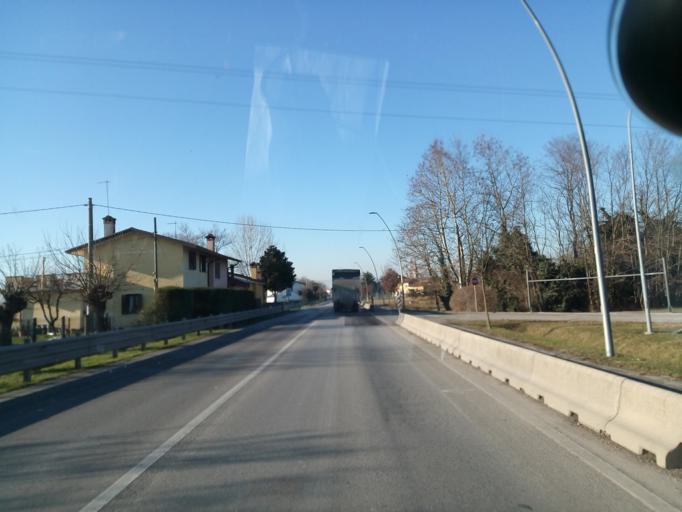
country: IT
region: Veneto
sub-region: Provincia di Treviso
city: Resana
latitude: 45.6268
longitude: 11.9626
